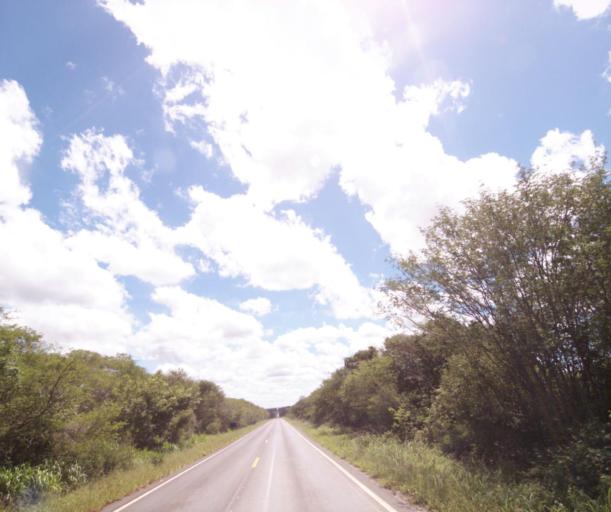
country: BR
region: Bahia
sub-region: Sao Felix Do Coribe
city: Santa Maria da Vitoria
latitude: -13.3606
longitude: -43.9758
